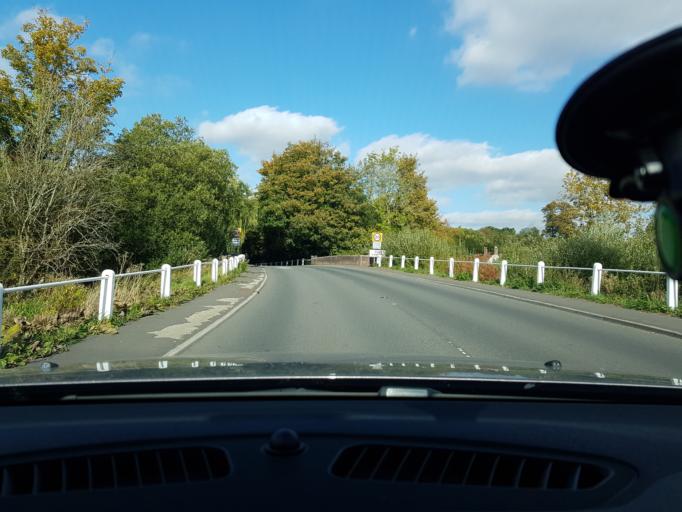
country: GB
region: England
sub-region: Wiltshire
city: Chilton Foliat
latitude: 51.4297
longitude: -1.5371
